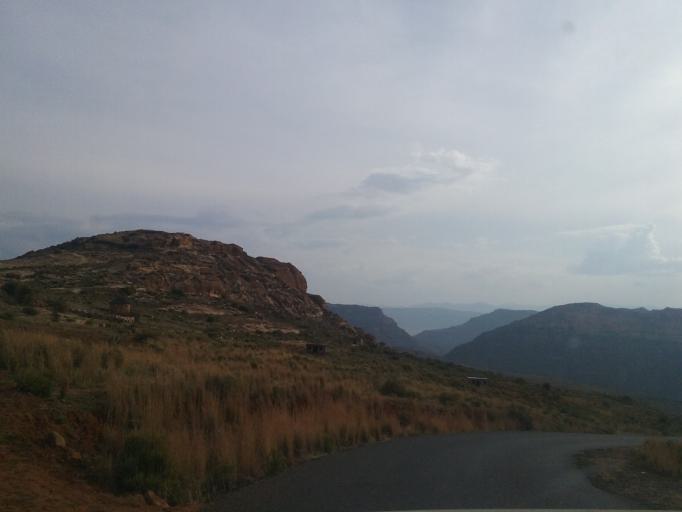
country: LS
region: Quthing
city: Quthing
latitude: -30.2208
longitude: 27.9158
